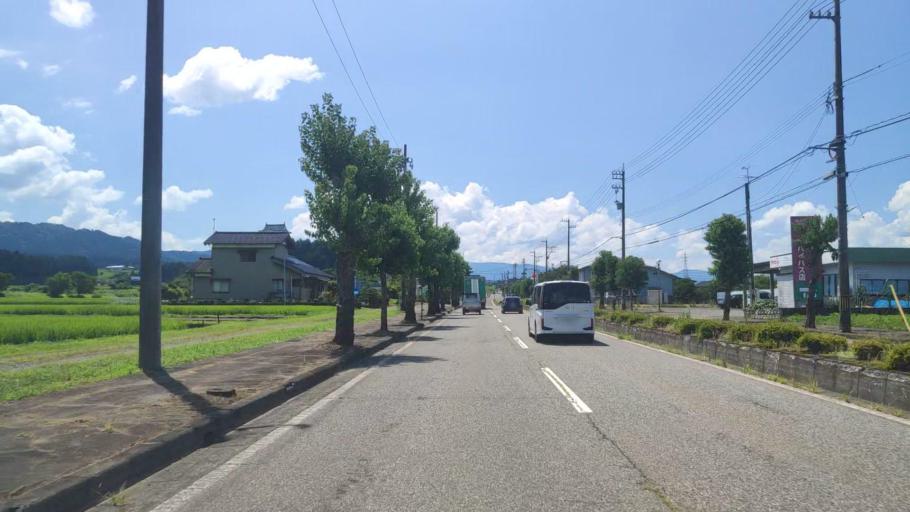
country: JP
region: Fukui
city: Katsuyama
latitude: 36.0470
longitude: 136.5161
